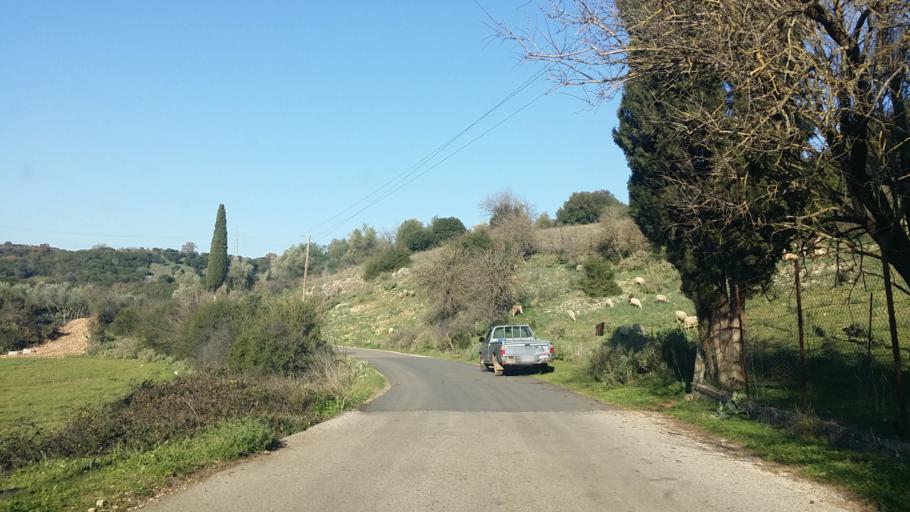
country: GR
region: West Greece
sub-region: Nomos Aitolias kai Akarnanias
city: Katouna
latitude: 38.7891
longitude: 21.1074
